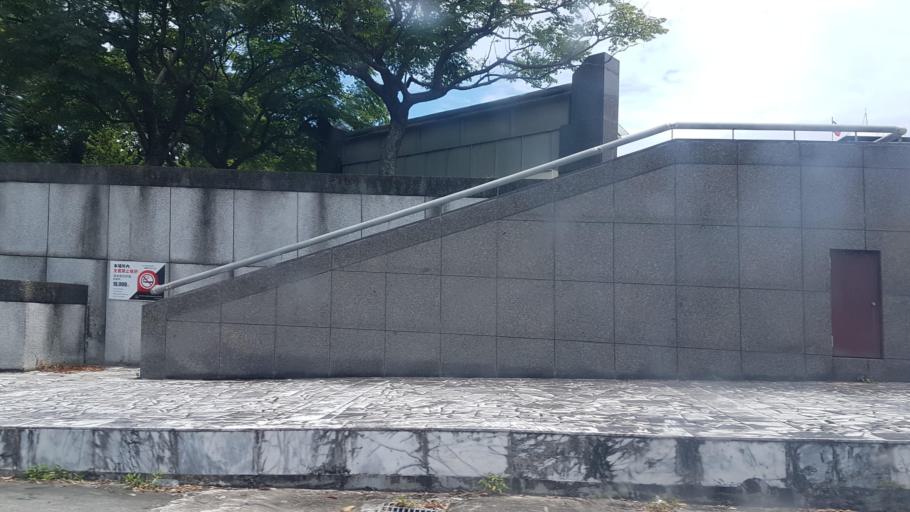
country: TW
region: Taiwan
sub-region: Hualien
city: Hualian
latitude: 23.9901
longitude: 121.6199
